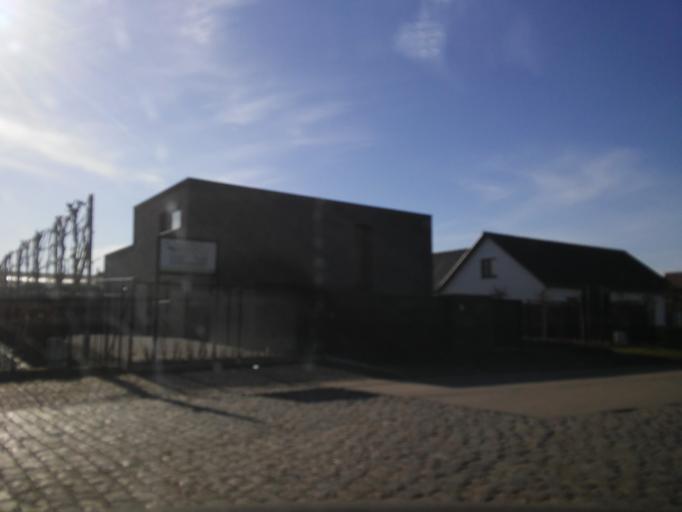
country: BE
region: Flanders
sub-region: Provincie Oost-Vlaanderen
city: Eeklo
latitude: 51.1757
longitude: 3.5058
